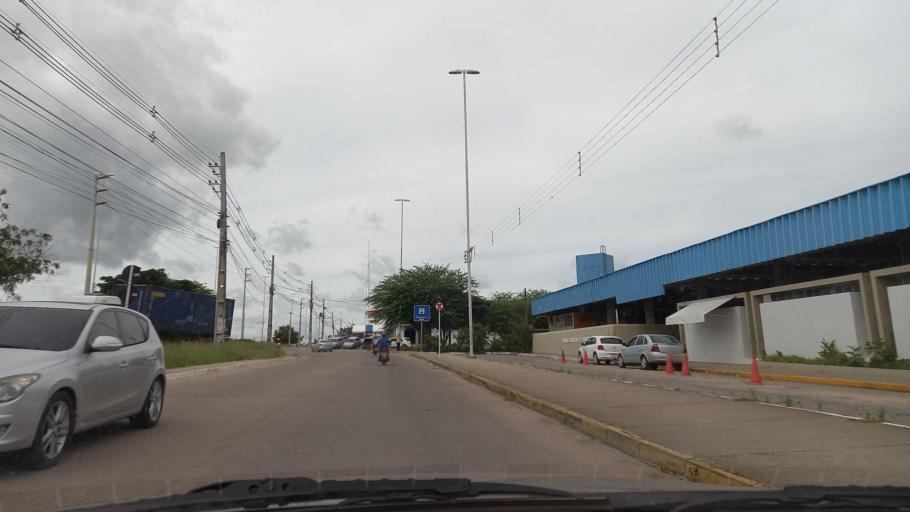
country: BR
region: Pernambuco
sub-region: Gravata
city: Gravata
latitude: -8.1963
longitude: -35.5694
